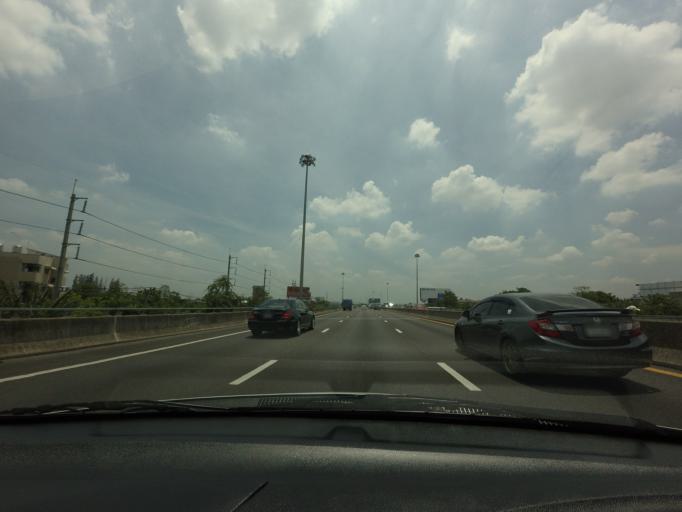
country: TH
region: Bangkok
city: Lat Phrao
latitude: 13.8203
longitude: 100.6252
